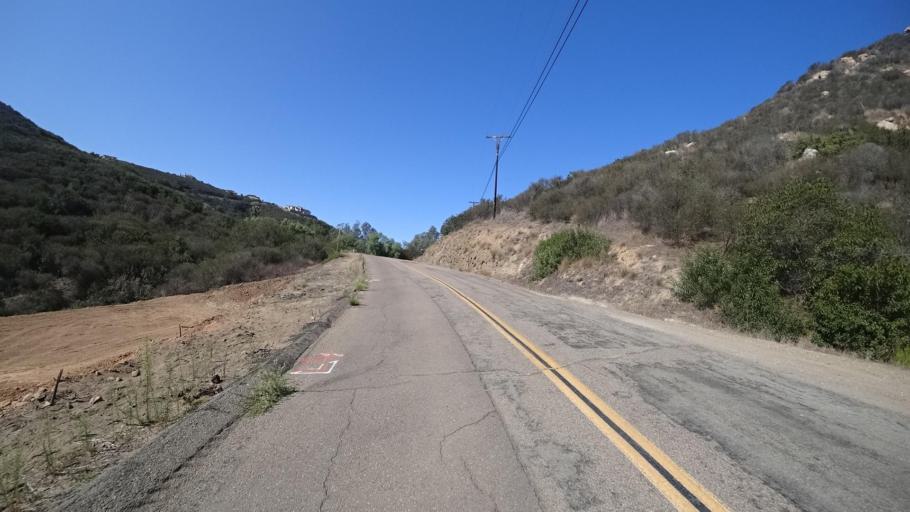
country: US
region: California
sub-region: San Diego County
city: Escondido
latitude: 33.0598
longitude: -117.1338
